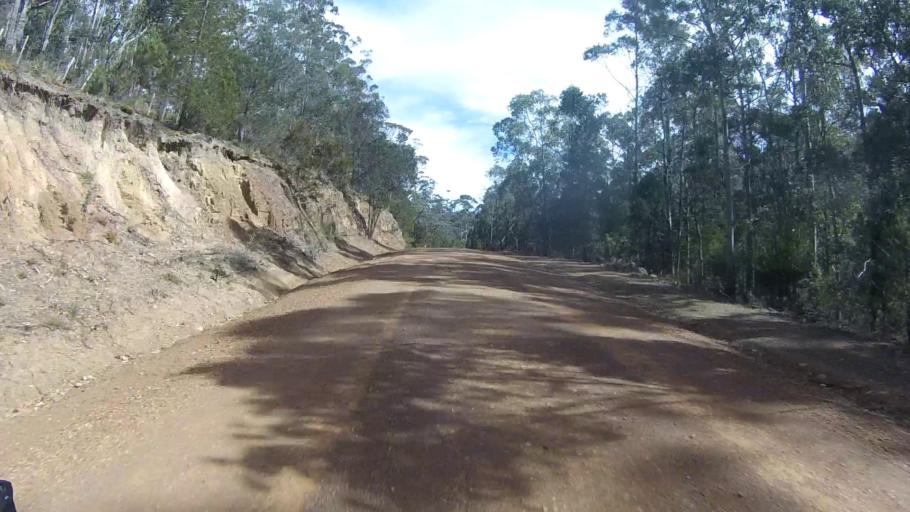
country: AU
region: Tasmania
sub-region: Sorell
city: Sorell
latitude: -42.6149
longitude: 147.8992
